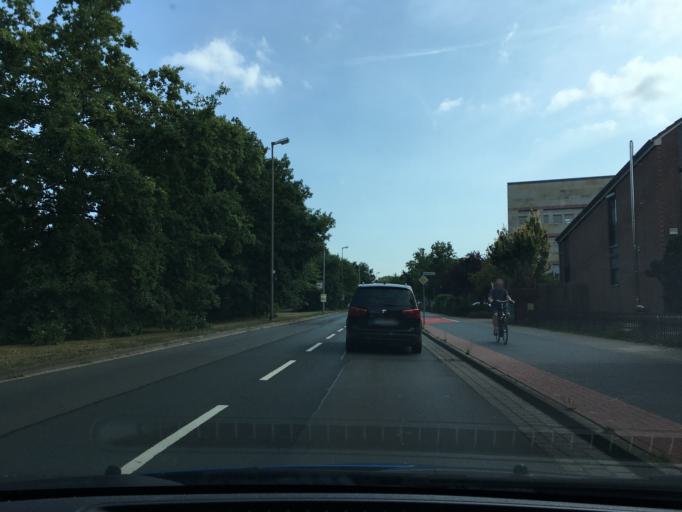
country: DE
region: Lower Saxony
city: Langenhagen
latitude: 52.4384
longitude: 9.7544
